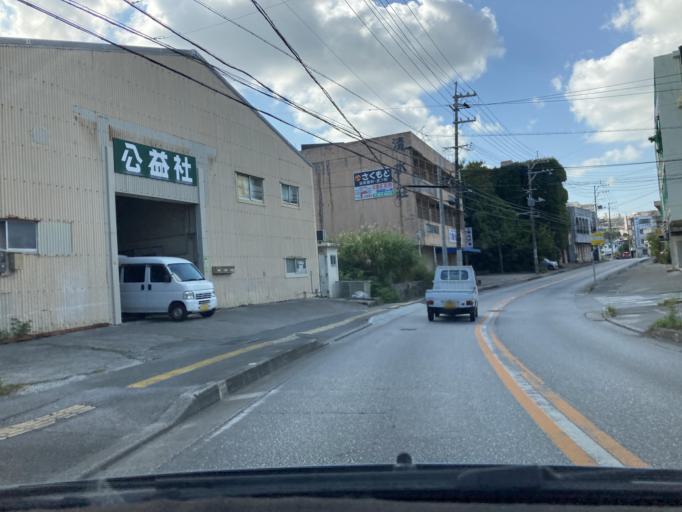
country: JP
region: Okinawa
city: Tomigusuku
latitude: 26.1809
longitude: 127.6853
